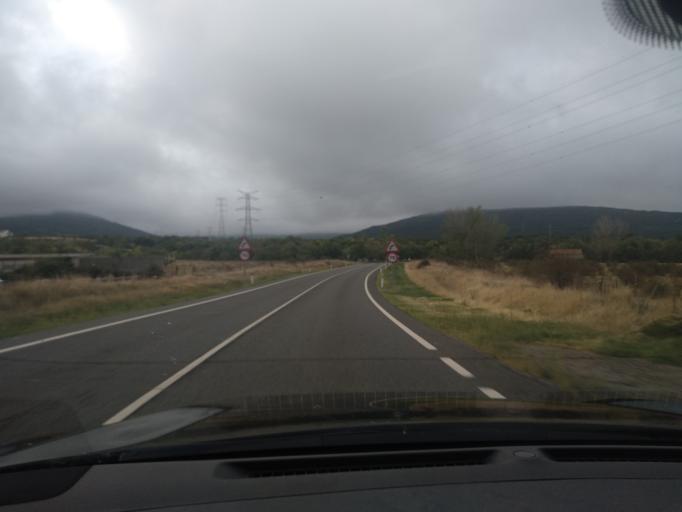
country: ES
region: Castille and Leon
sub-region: Provincia de Segovia
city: Otero de Herreros
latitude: 40.7468
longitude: -4.1992
